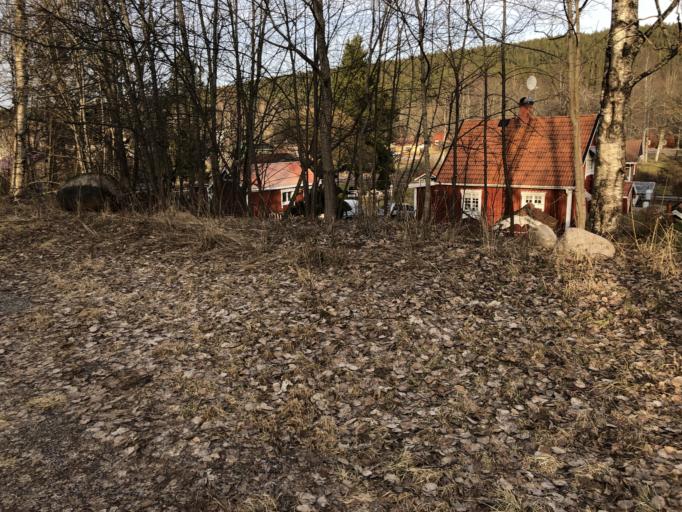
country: SE
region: Vaermland
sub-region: Filipstads Kommun
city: Lesjofors
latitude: 59.9769
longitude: 14.1813
